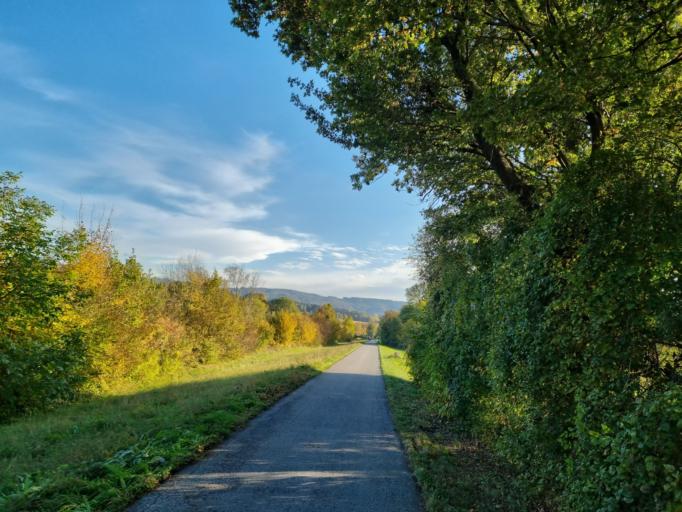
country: AT
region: Lower Austria
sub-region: Politischer Bezirk Sankt Polten
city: Pyhra
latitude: 48.1479
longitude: 15.6390
